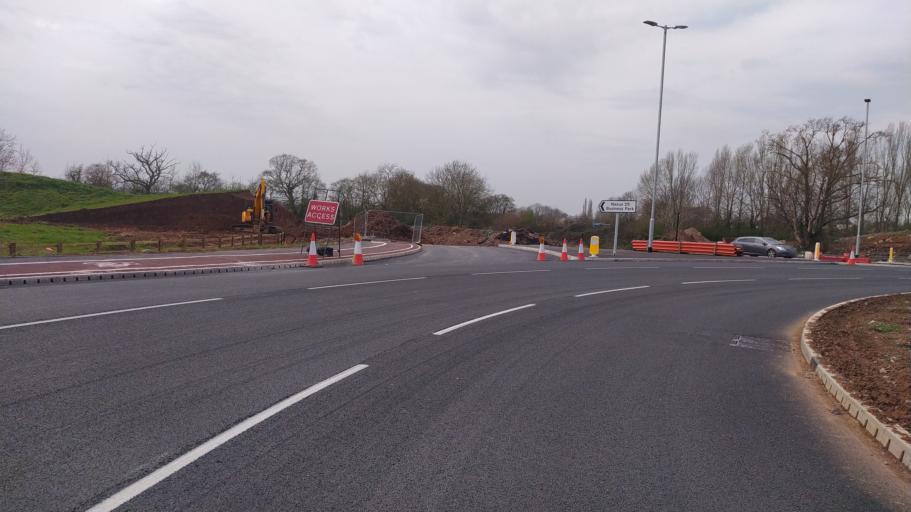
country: GB
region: England
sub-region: Somerset
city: Creech Saint Michael
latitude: 51.0152
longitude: -3.0598
